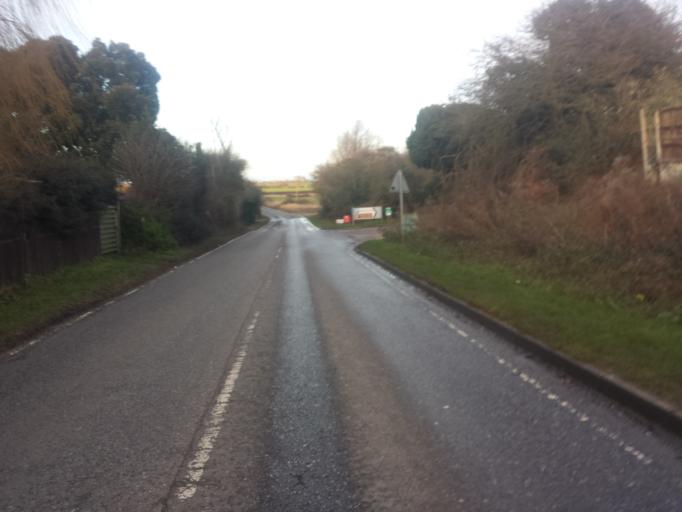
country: GB
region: England
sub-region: Essex
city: Frinton-on-Sea
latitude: 51.8066
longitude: 1.2039
